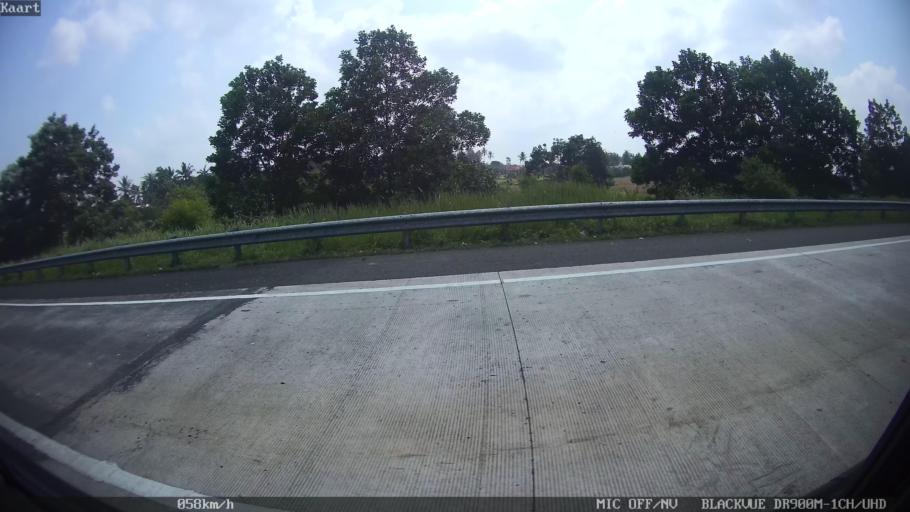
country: ID
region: Lampung
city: Kedaton
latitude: -5.3504
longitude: 105.3218
